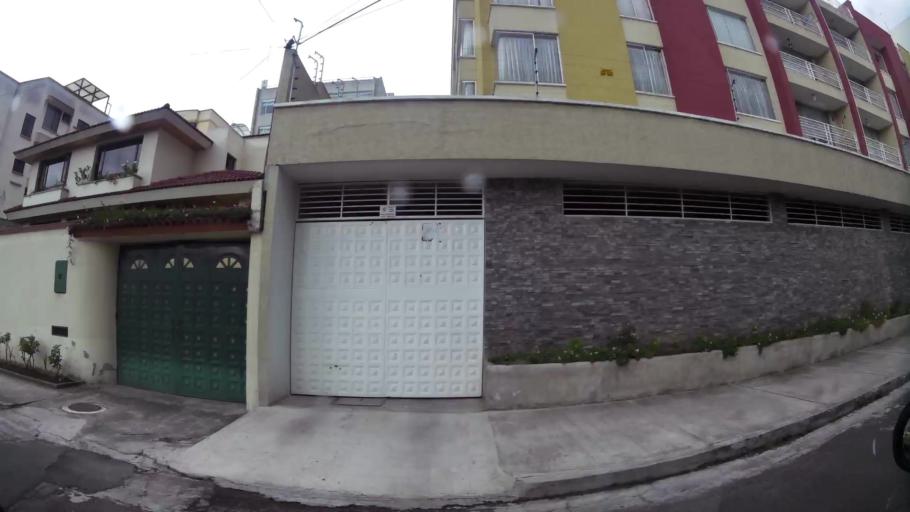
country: EC
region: Pichincha
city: Quito
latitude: -0.1008
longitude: -78.4821
